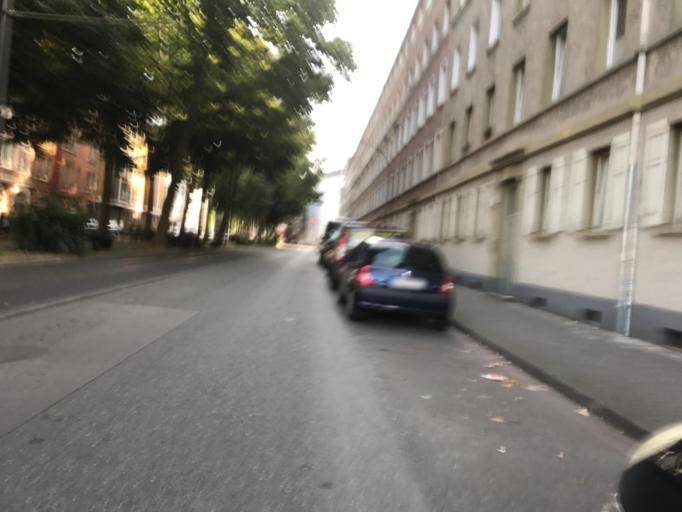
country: DE
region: Rheinland-Pfalz
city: Mainz
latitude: 50.0149
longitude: 8.2504
